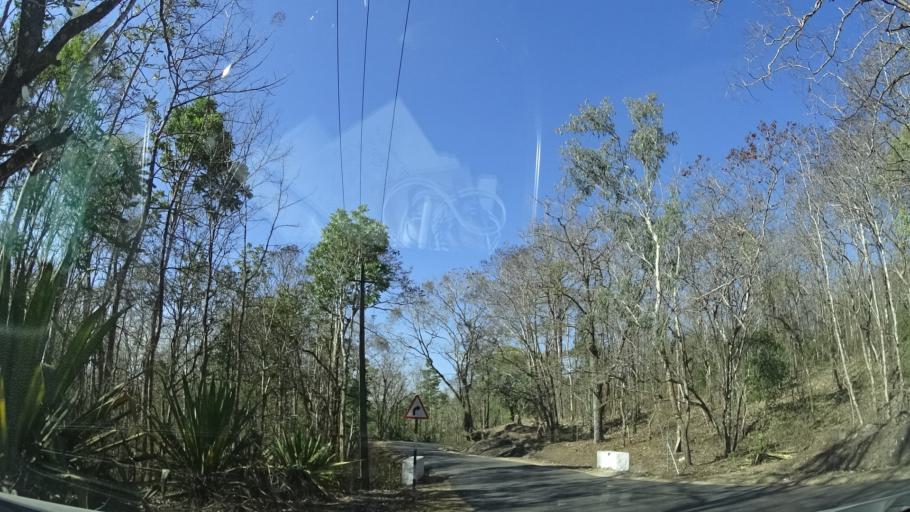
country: IN
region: Karnataka
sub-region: Chikmagalur
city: Koppa
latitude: 13.3585
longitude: 75.5008
